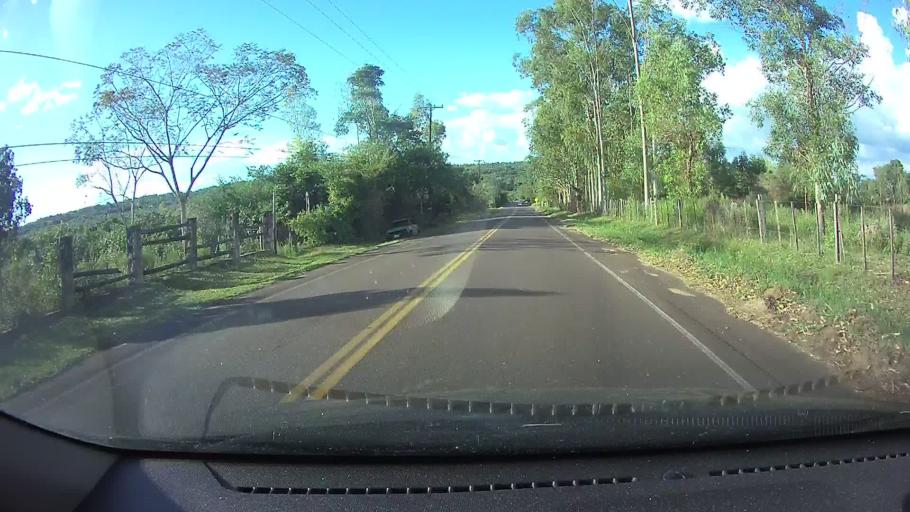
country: PY
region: Cordillera
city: Altos
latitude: -25.1926
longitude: -57.2242
